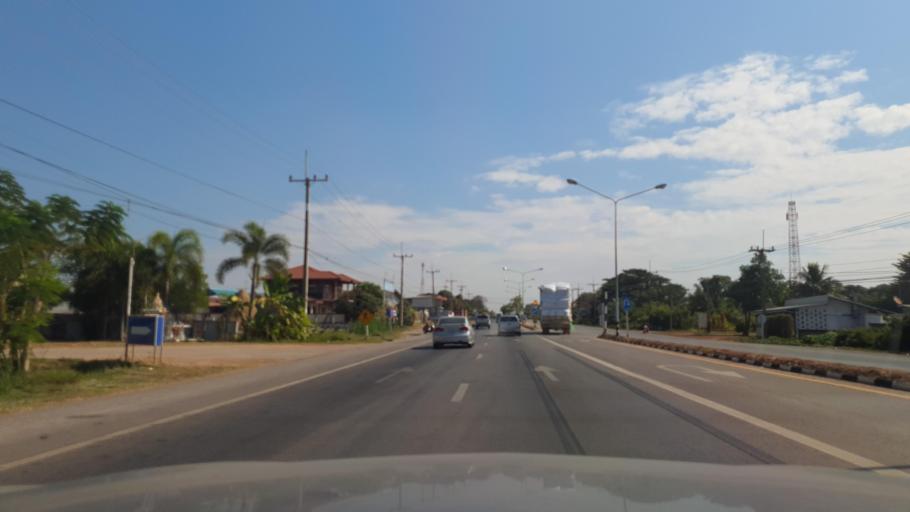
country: TH
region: Maha Sarakham
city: Chiang Yuen
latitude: 16.3781
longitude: 103.1831
